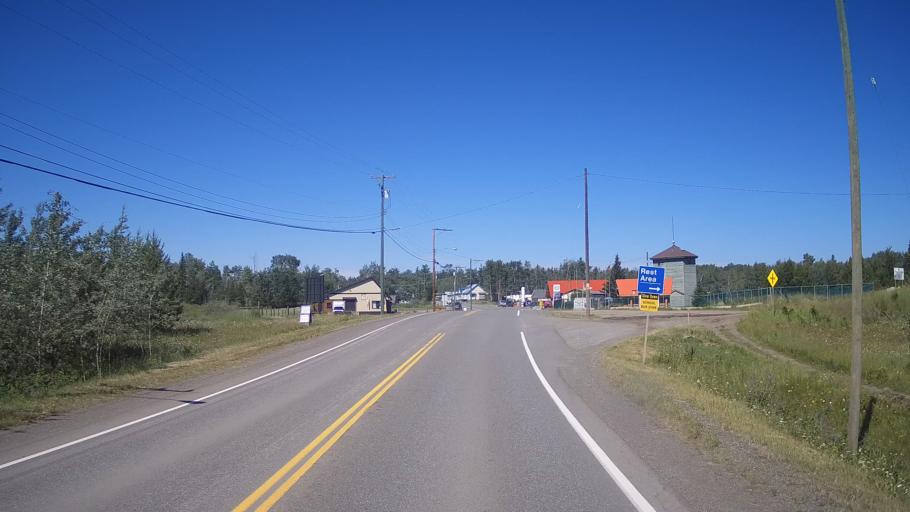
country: CA
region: British Columbia
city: Cache Creek
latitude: 51.5548
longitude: -121.2025
